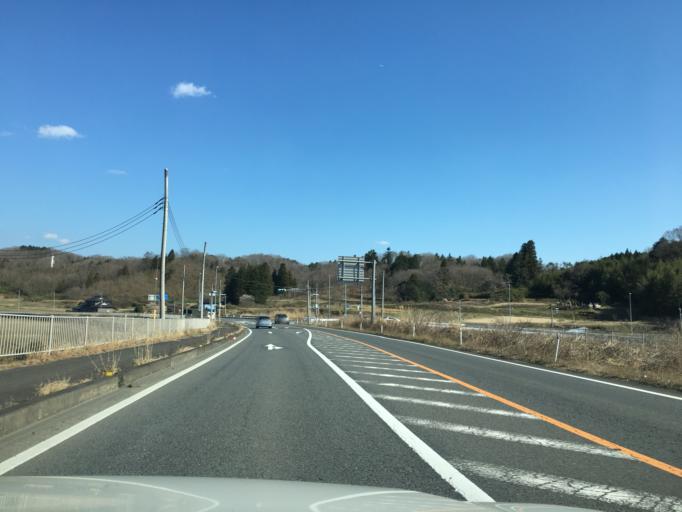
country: JP
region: Tochigi
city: Motegi
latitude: 36.5247
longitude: 140.1878
